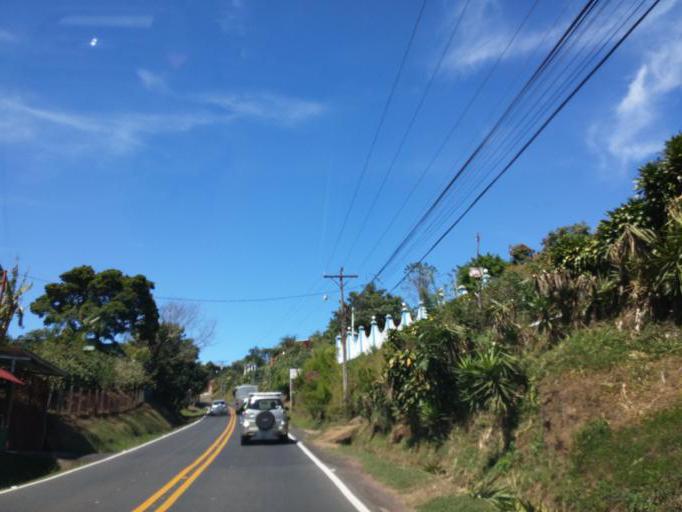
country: CR
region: Alajuela
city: Sabanilla
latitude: 10.0899
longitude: -84.1885
